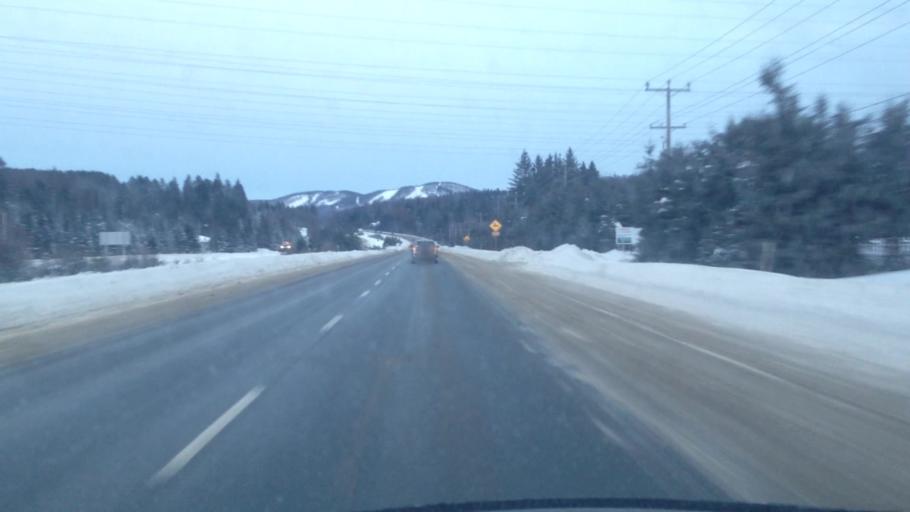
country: CA
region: Quebec
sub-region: Laurentides
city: Mont-Tremblant
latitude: 46.1151
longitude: -74.5482
